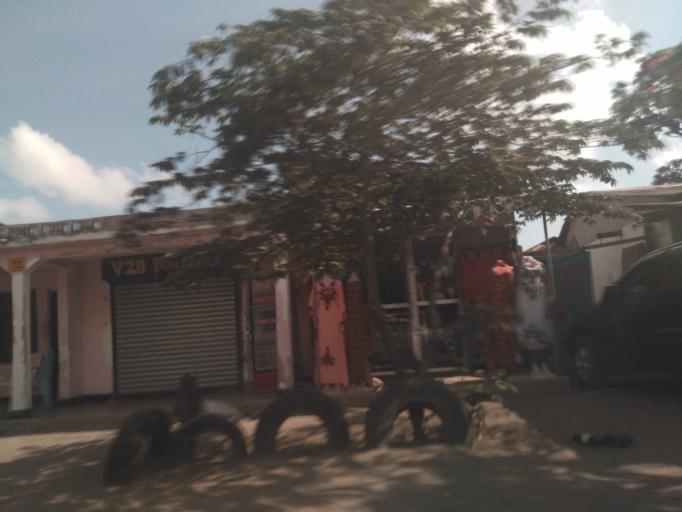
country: TZ
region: Dar es Salaam
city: Magomeni
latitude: -6.7905
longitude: 39.2553
